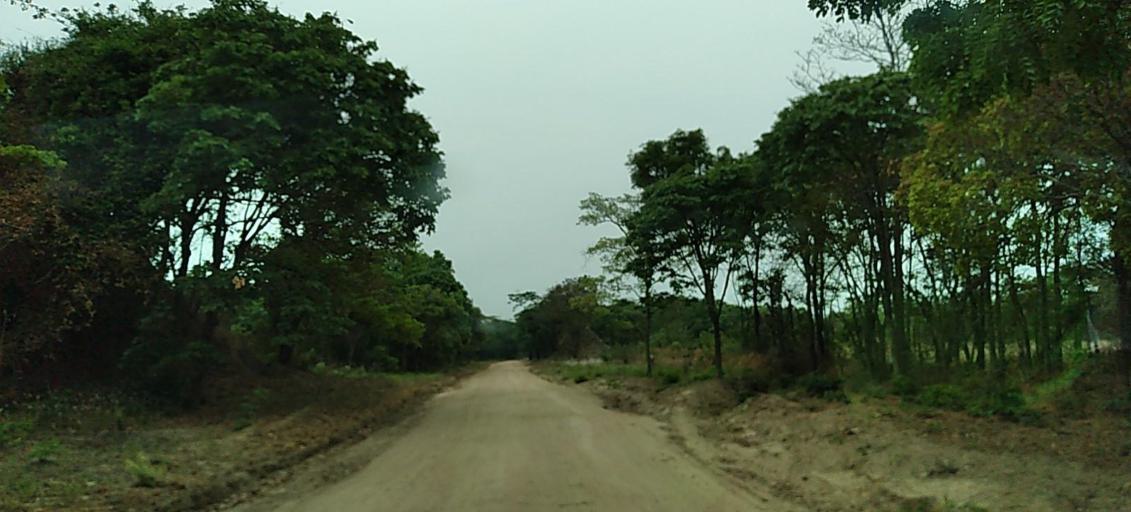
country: ZM
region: North-Western
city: Solwezi
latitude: -12.5299
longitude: 26.5230
